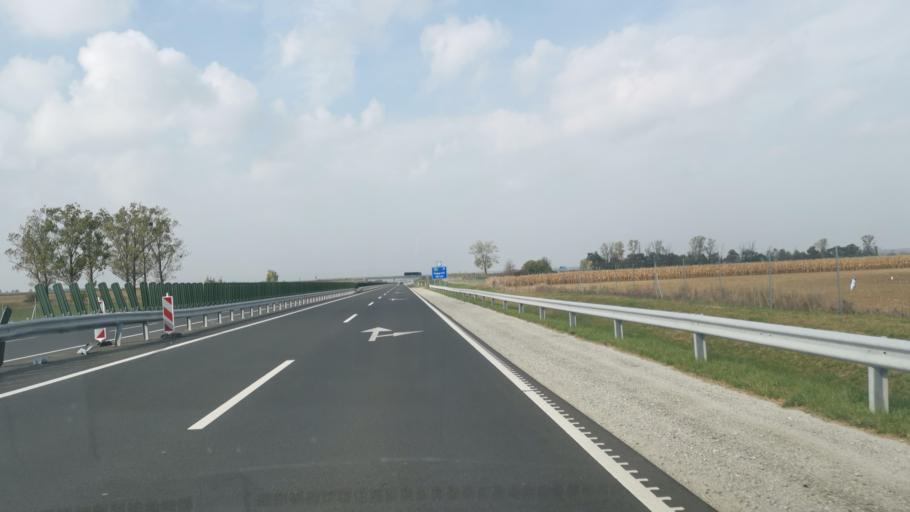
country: HU
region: Gyor-Moson-Sopron
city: Nagycenk
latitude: 47.5867
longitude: 16.7152
